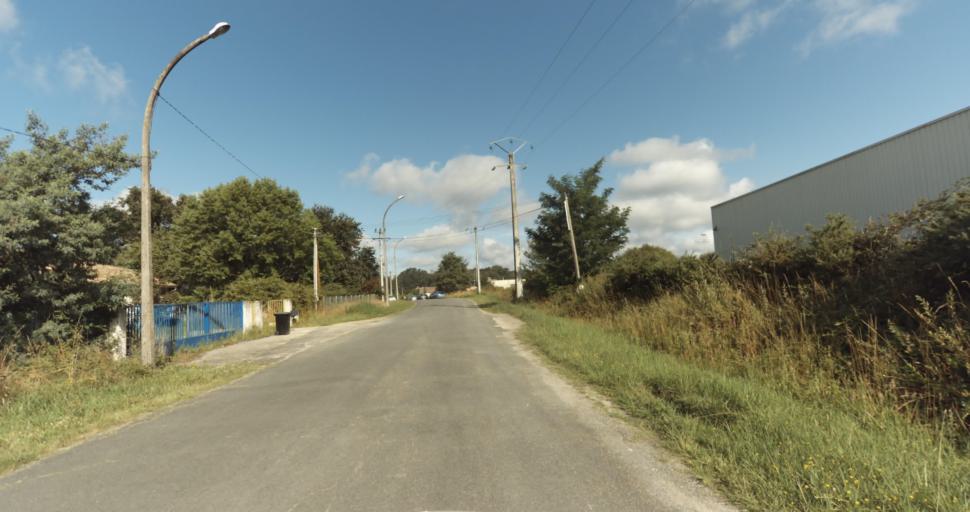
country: FR
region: Aquitaine
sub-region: Departement de la Gironde
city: Bazas
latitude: 44.4379
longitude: -0.2342
